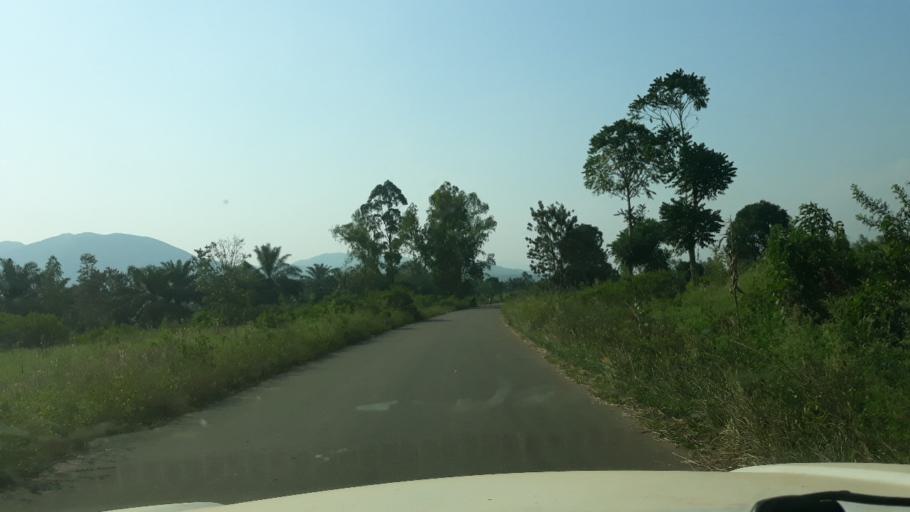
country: BI
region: Cibitoke
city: Cibitoke
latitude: -2.7673
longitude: 28.9997
